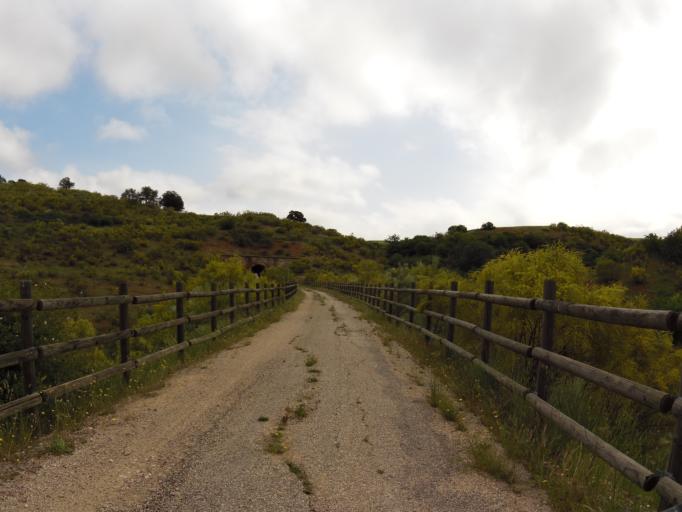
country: ES
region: Castille-La Mancha
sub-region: Provincia de Albacete
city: Alcaraz
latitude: 38.7116
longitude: -2.4952
